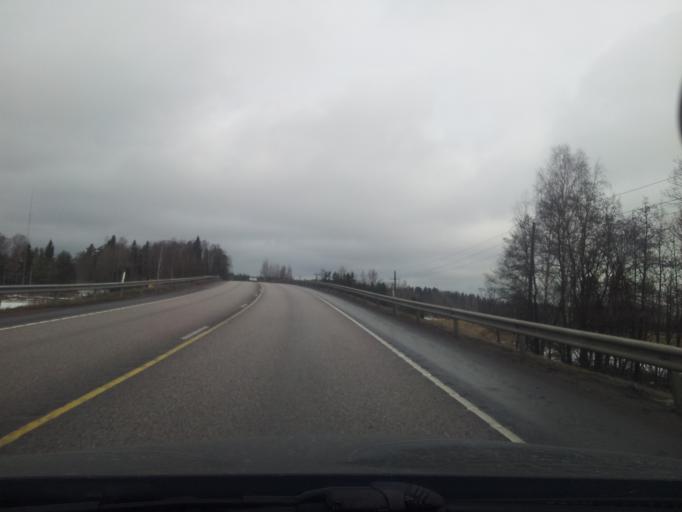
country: FI
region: Uusimaa
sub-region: Helsinki
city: Espoo
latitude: 60.1762
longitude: 24.5591
